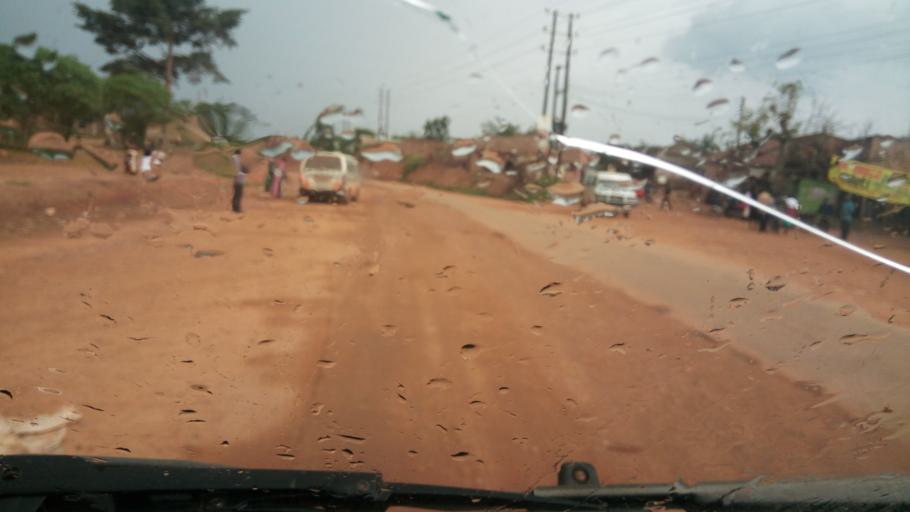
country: UG
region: Central Region
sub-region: Wakiso District
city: Wakiso
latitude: 0.4575
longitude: 32.3339
